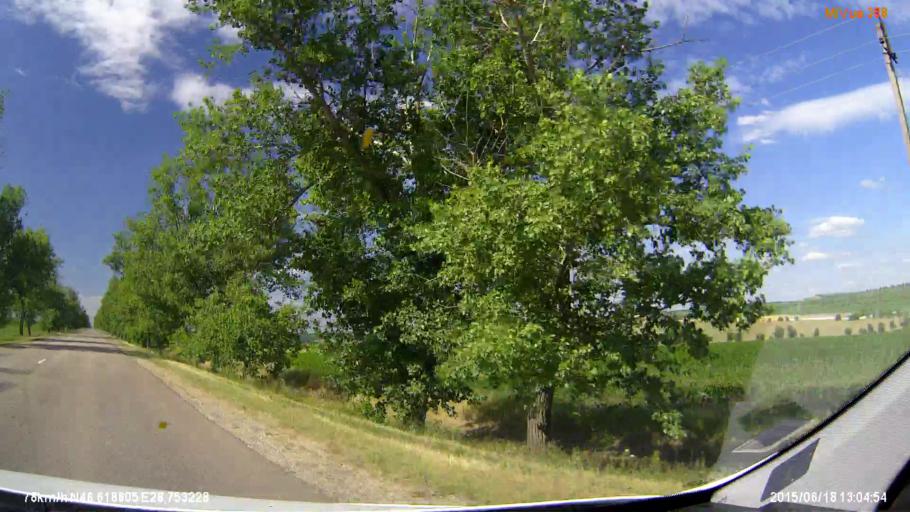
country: MD
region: Cimislia
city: Cimislia
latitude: 46.6184
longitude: 28.7532
